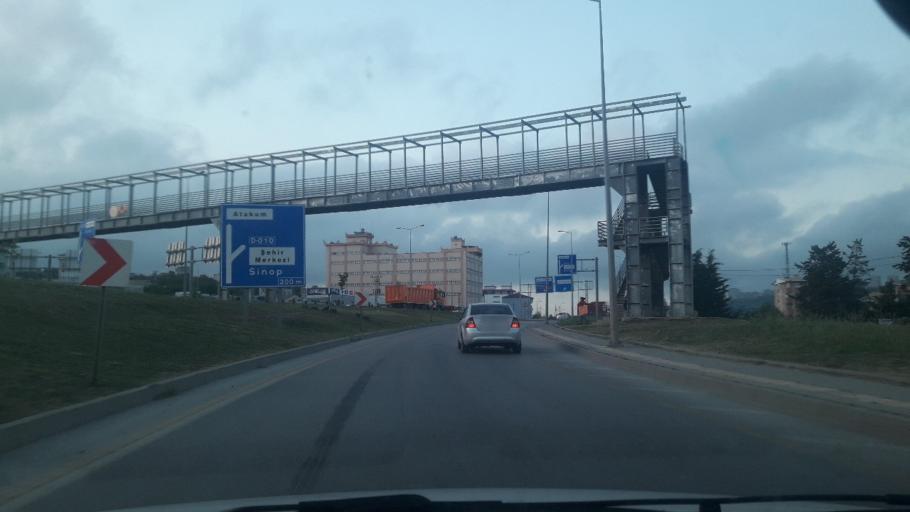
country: TR
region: Samsun
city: Samsun
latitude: 41.2914
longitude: 36.2885
